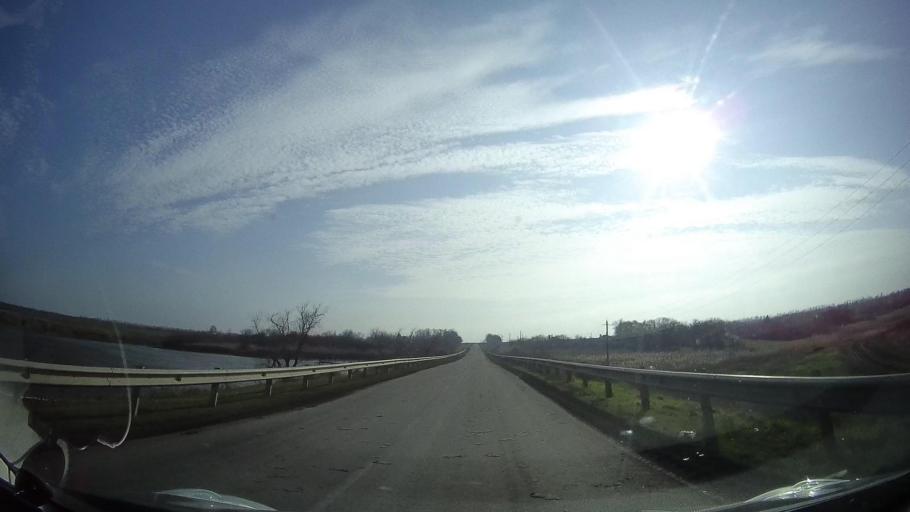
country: RU
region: Rostov
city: Mechetinskaya
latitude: 46.9128
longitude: 40.5355
